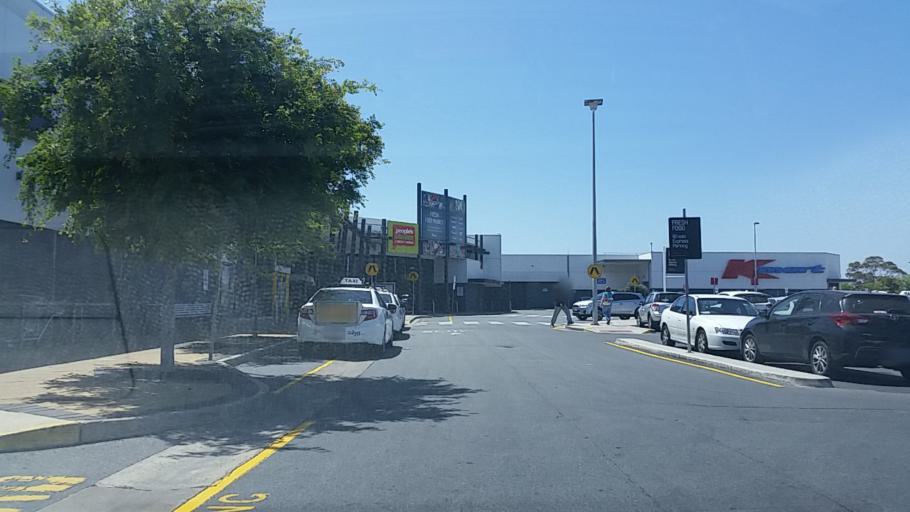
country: AU
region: South Australia
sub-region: Charles Sturt
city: Grange
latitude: -34.8813
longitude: 138.4922
